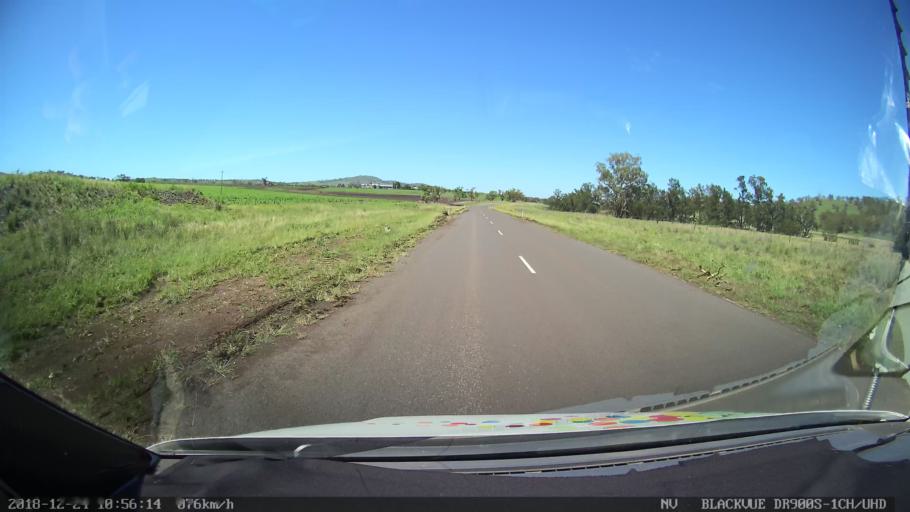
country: AU
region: New South Wales
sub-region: Upper Hunter Shire
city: Merriwa
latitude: -32.0234
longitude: 150.4190
